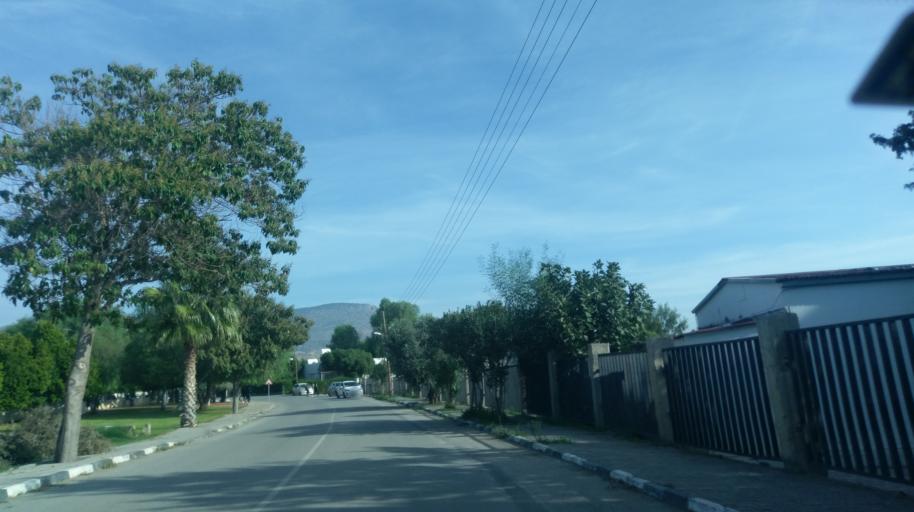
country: CY
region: Lefkosia
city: Nicosia
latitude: 35.2362
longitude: 33.4837
